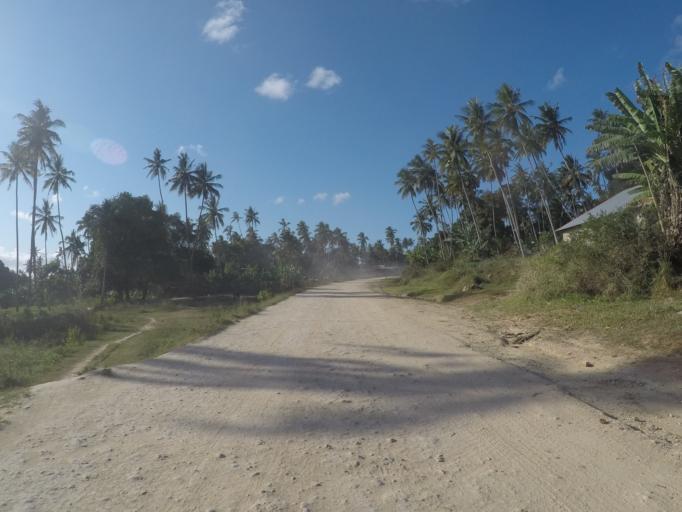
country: TZ
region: Zanzibar Central/South
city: Koani
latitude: -6.1776
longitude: 39.2833
